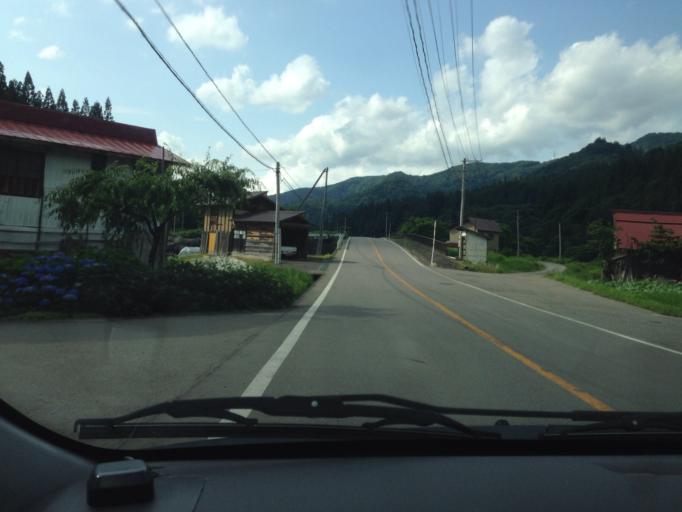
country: JP
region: Fukushima
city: Kitakata
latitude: 37.4079
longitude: 139.5512
